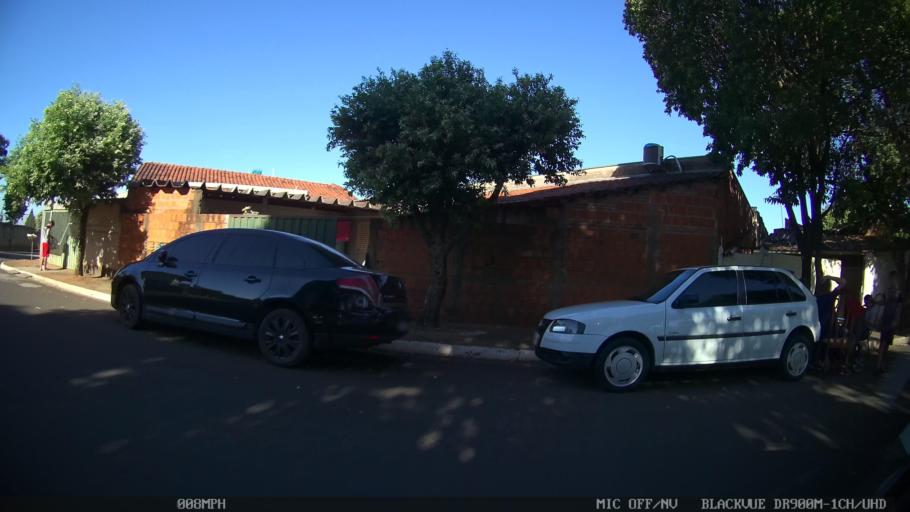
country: BR
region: Sao Paulo
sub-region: Olimpia
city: Olimpia
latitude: -20.7427
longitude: -48.8902
